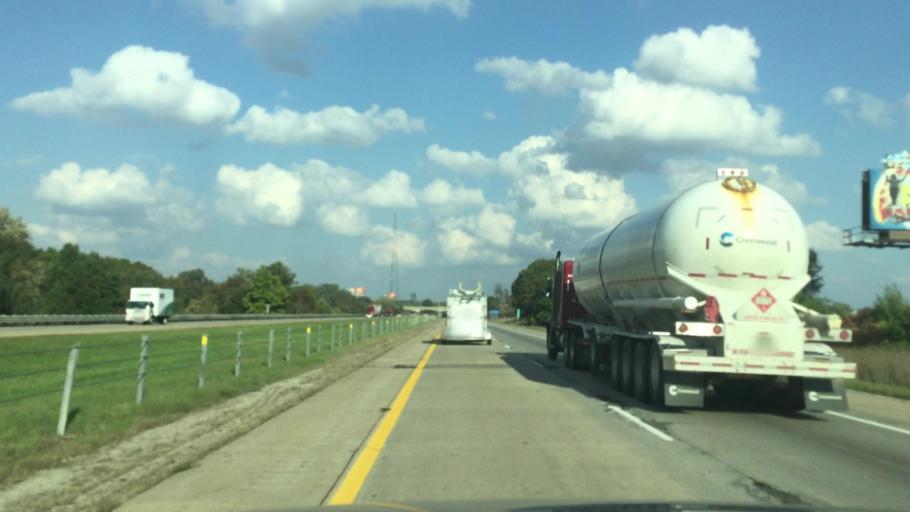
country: US
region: Michigan
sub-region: Calhoun County
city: Brownlee Park
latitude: 42.2964
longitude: -85.0955
